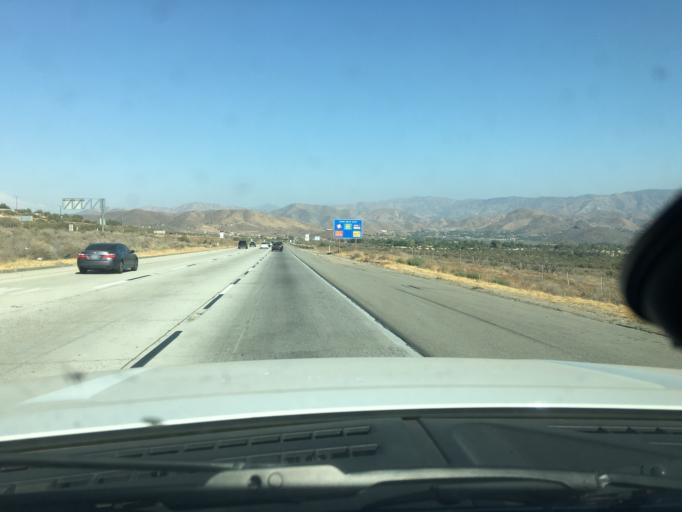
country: US
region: California
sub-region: Los Angeles County
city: Acton
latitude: 34.4941
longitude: -118.2132
